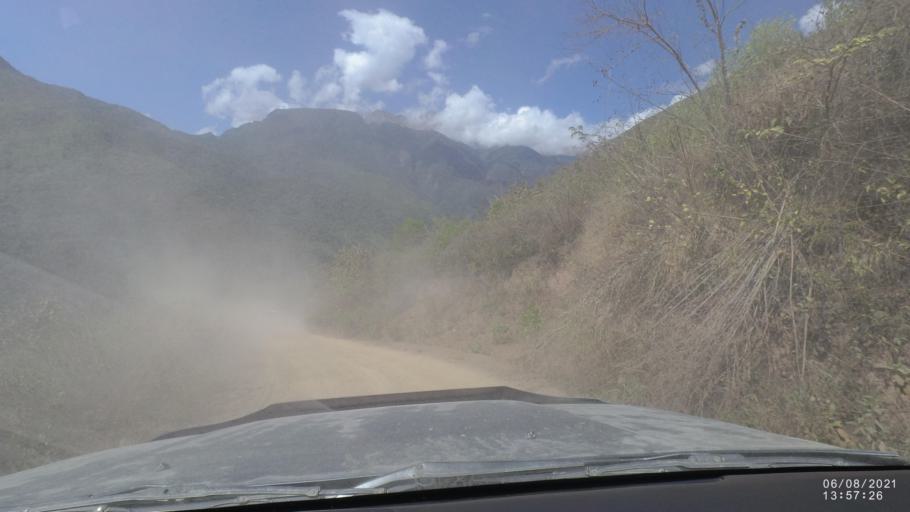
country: BO
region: La Paz
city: Quime
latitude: -16.6444
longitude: -66.7291
